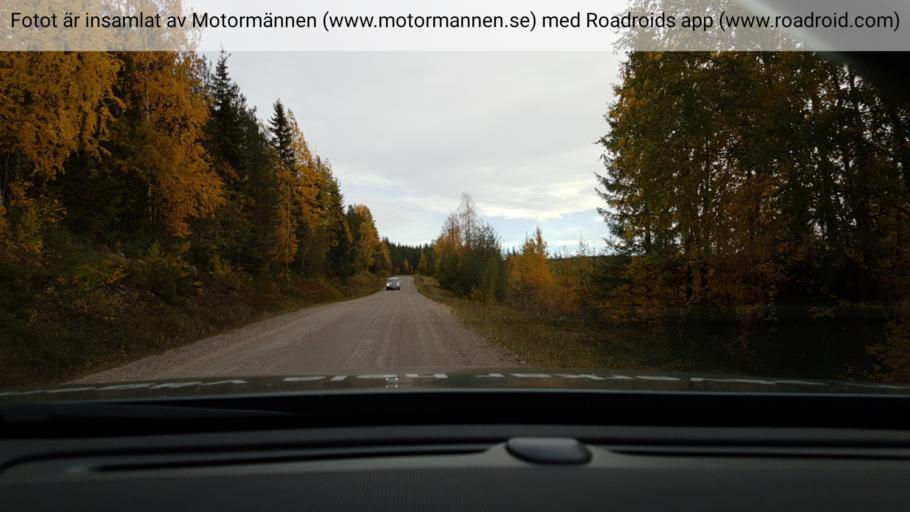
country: SE
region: Norrbotten
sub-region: Overkalix Kommun
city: OEverkalix
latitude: 66.2653
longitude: 23.0170
